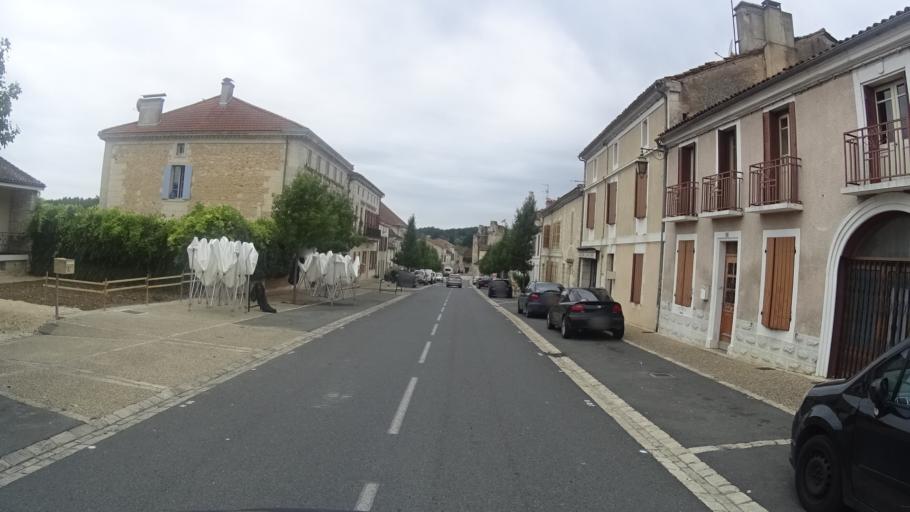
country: FR
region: Aquitaine
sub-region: Departement de la Dordogne
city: Neuvic
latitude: 45.0217
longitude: 0.5395
